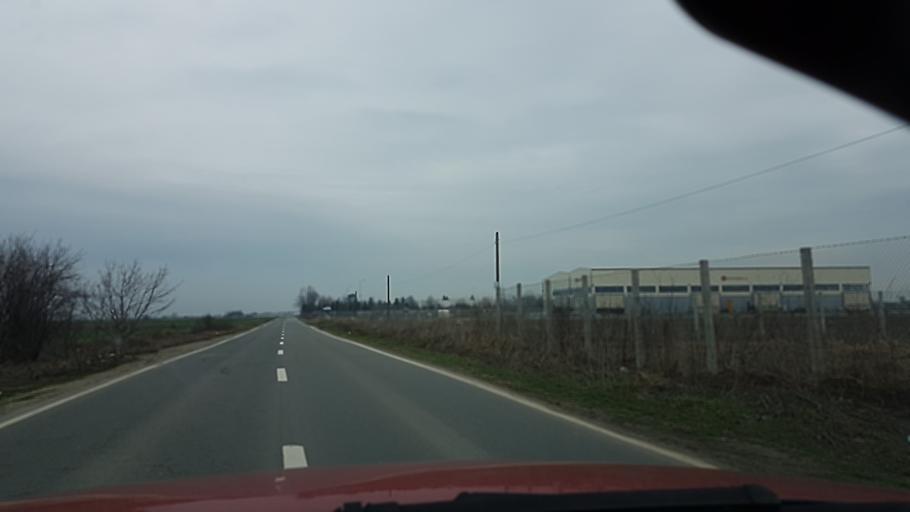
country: RO
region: Ilfov
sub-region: Comuna Balotesti
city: Balotesti
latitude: 44.6122
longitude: 26.1280
